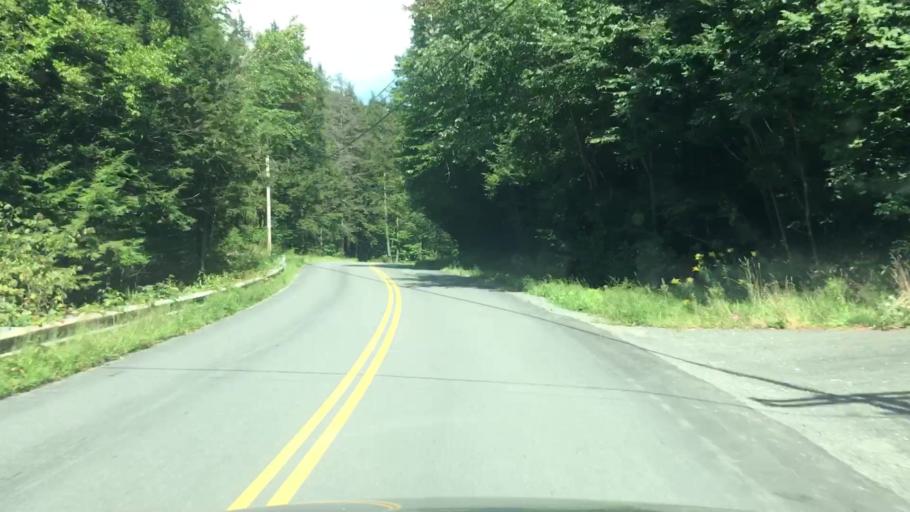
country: US
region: Vermont
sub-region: Windham County
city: West Brattleboro
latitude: 42.8019
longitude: -72.6189
